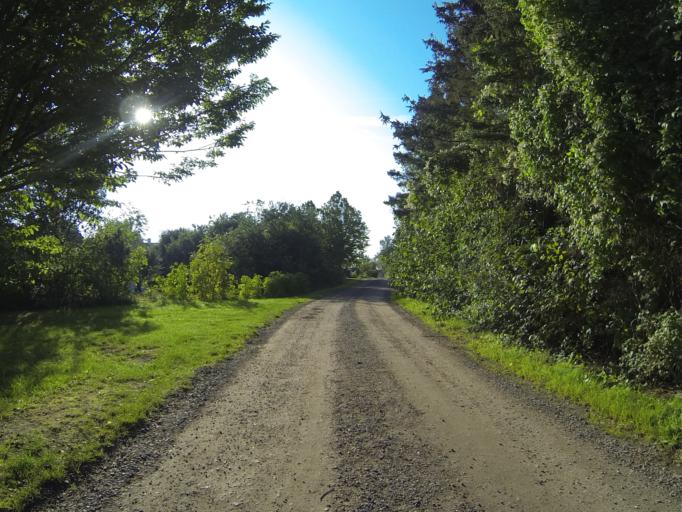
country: SE
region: Skane
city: Smygehamn
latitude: 55.3460
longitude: 13.3730
